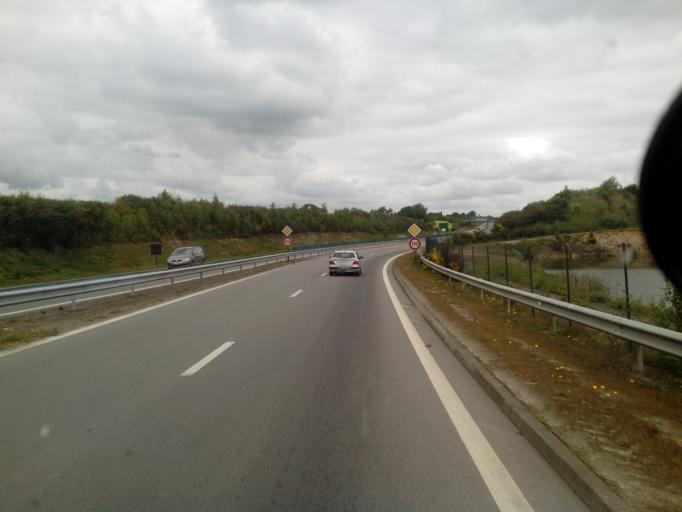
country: FR
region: Brittany
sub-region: Departement d'Ille-et-Vilaine
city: Betton
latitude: 48.1557
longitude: -1.6250
